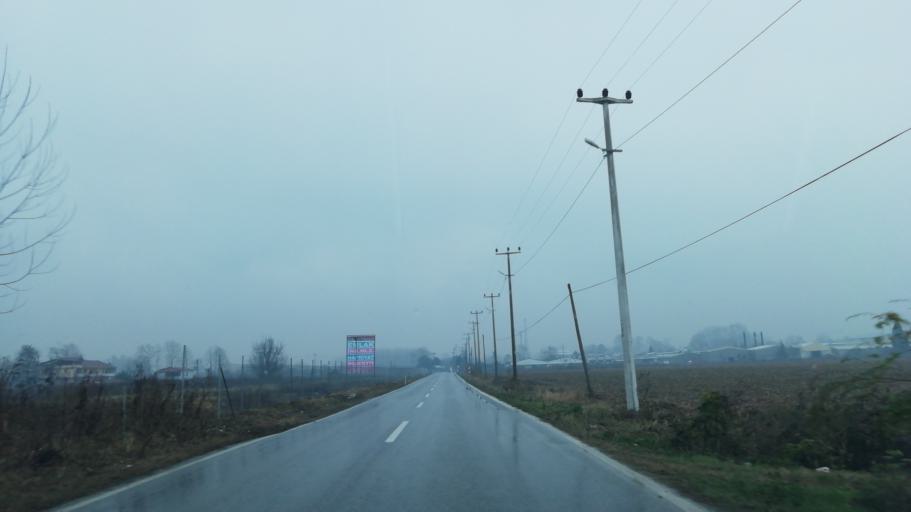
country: TR
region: Sakarya
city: Akyazi
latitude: 40.6720
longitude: 30.5797
